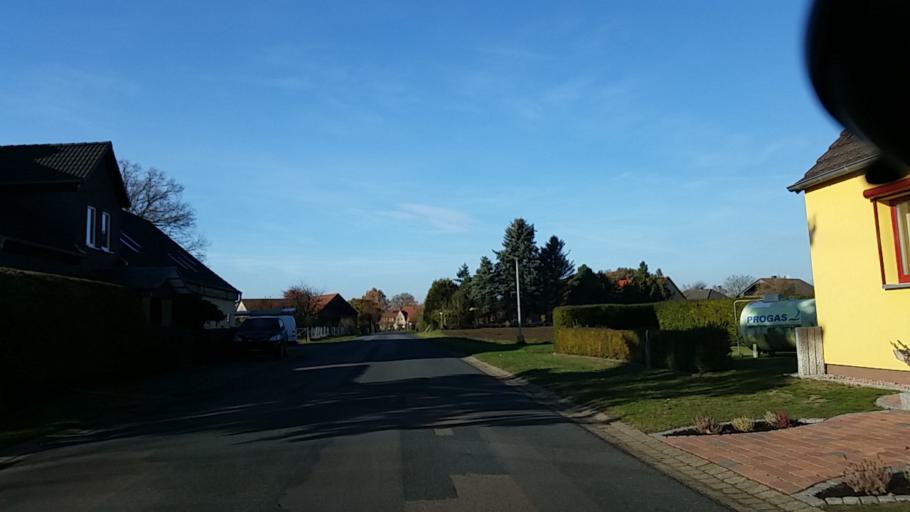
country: DE
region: Lower Saxony
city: Tulau
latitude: 52.6139
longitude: 10.8735
